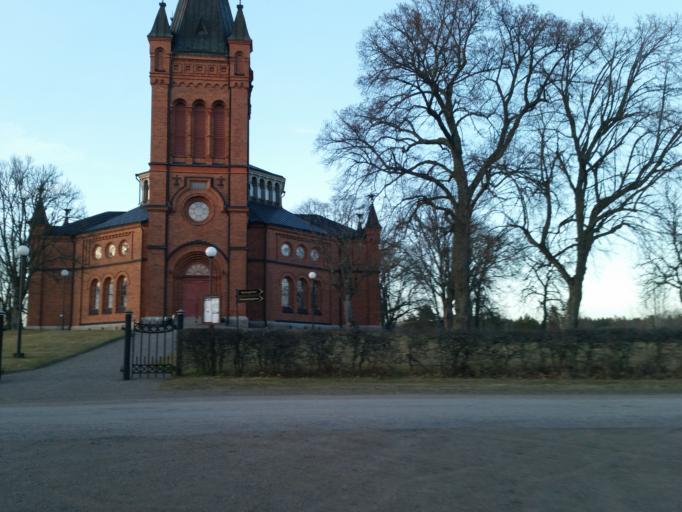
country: SE
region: Kalmar
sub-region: Vasterviks Kommun
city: Ankarsrum
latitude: 57.7091
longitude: 16.4522
